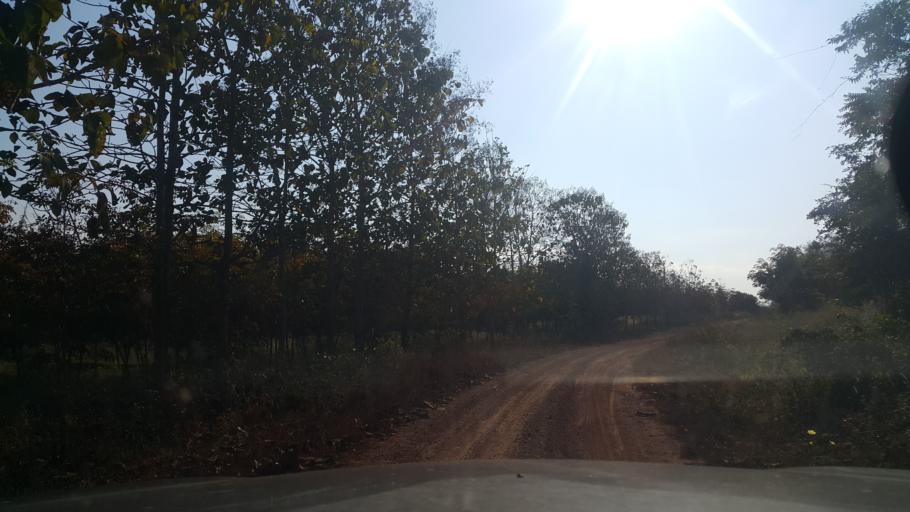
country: TH
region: Loei
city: Chiang Khan
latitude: 17.8279
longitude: 101.6143
